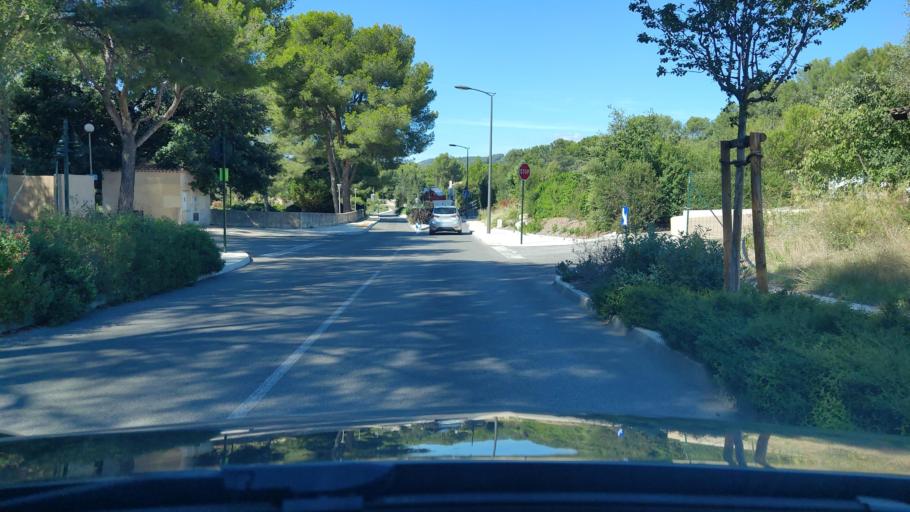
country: FR
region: Provence-Alpes-Cote d'Azur
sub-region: Departement du Var
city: Sanary-sur-Mer
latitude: 43.1413
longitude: 5.7800
